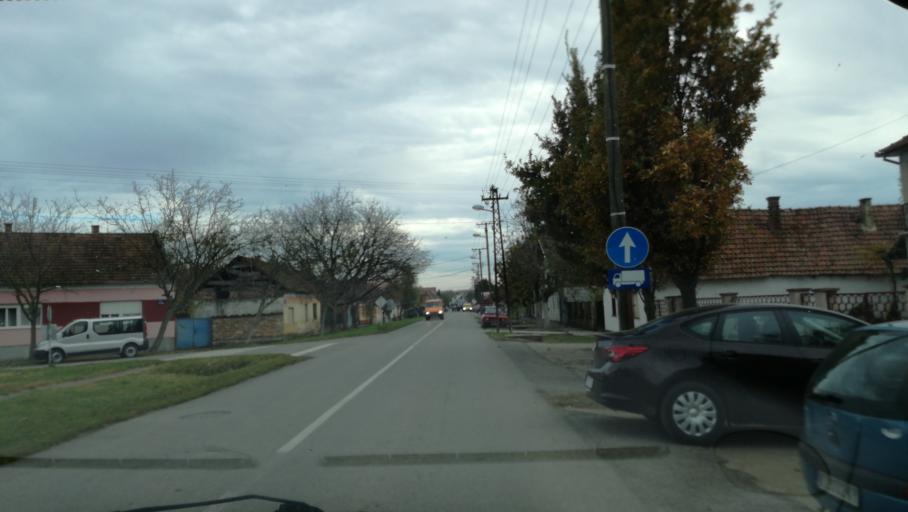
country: RS
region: Autonomna Pokrajina Vojvodina
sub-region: Severnobanatski Okrug
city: Kikinda
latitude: 45.8403
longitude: 20.4688
